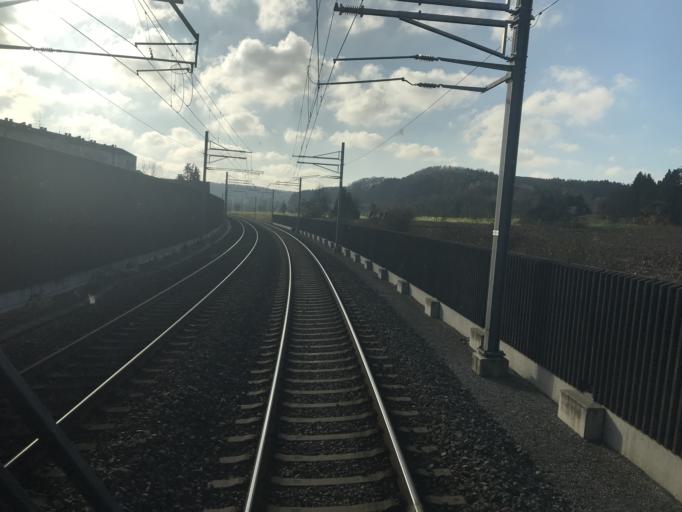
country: DE
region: Baden-Wuerttemberg
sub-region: Freiburg Region
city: Jestetten
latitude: 47.6522
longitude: 8.5652
